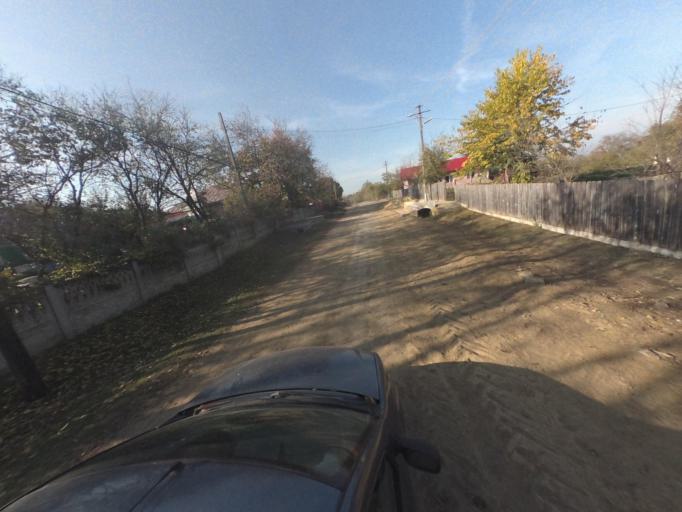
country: RO
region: Vaslui
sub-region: Comuna Bacesti
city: Bacesti
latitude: 46.8707
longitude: 27.2004
